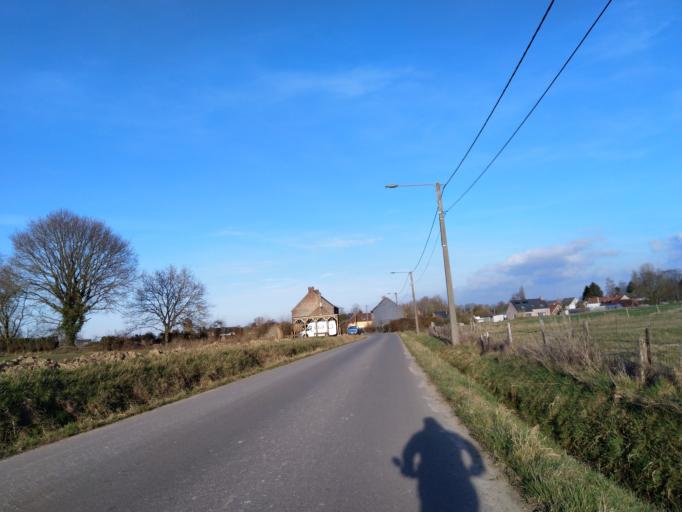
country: FR
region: Nord-Pas-de-Calais
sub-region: Departement du Nord
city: Feignies
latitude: 50.3334
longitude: 3.8951
